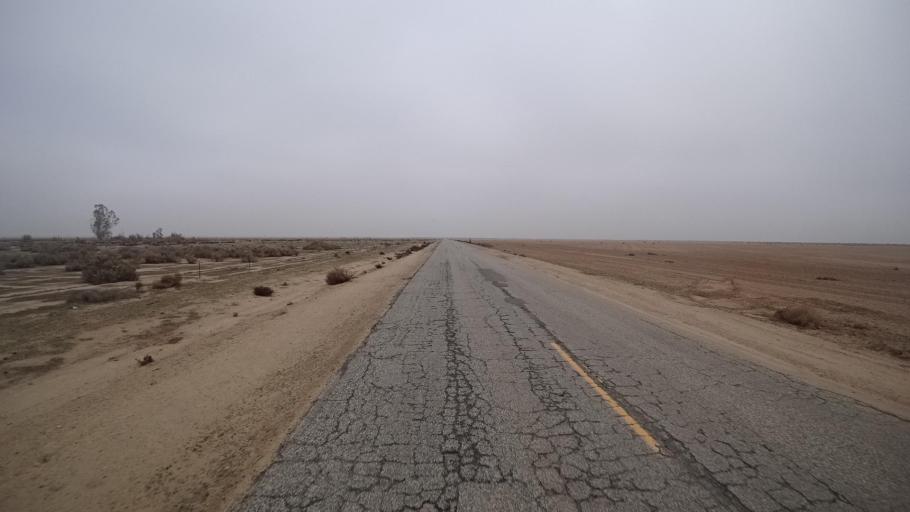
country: US
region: California
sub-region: Kern County
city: Maricopa
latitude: 35.1228
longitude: -119.2857
